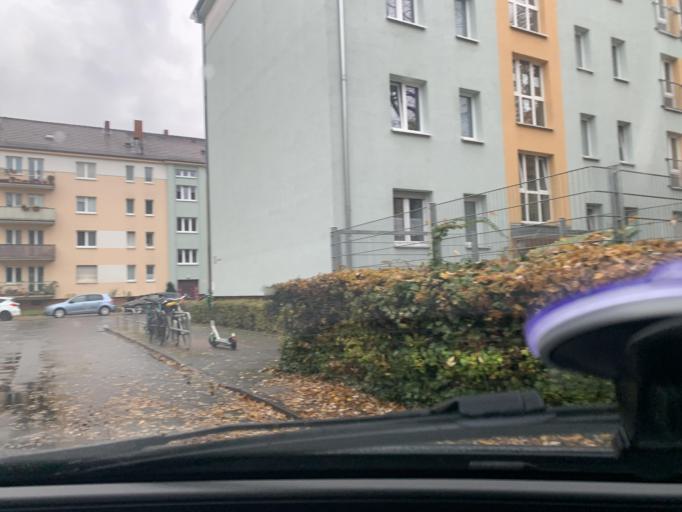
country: DE
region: Hesse
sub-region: Regierungsbezirk Darmstadt
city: Frankfurt am Main
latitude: 50.1213
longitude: 8.7114
